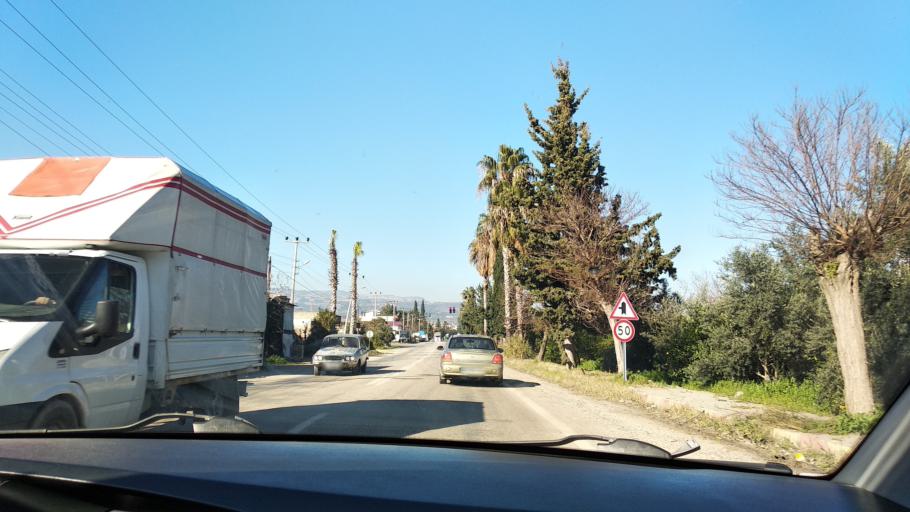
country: TR
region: Mersin
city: Tomuk
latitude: 36.6603
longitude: 34.3650
